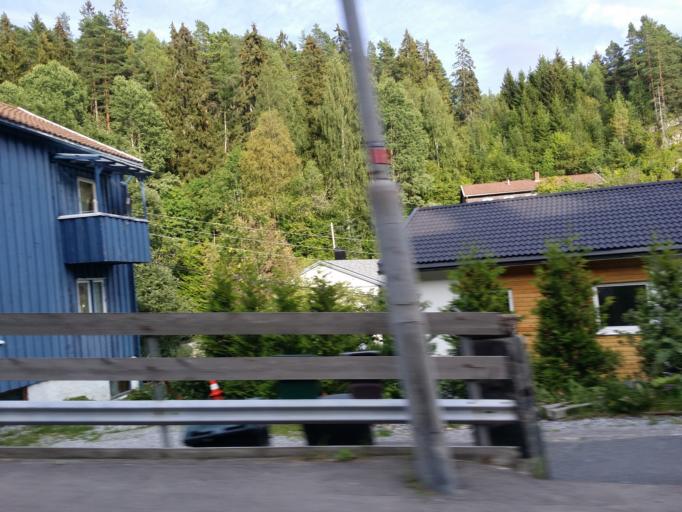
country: NO
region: Akershus
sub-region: Oppegard
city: Kolbotn
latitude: 59.8935
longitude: 10.8565
